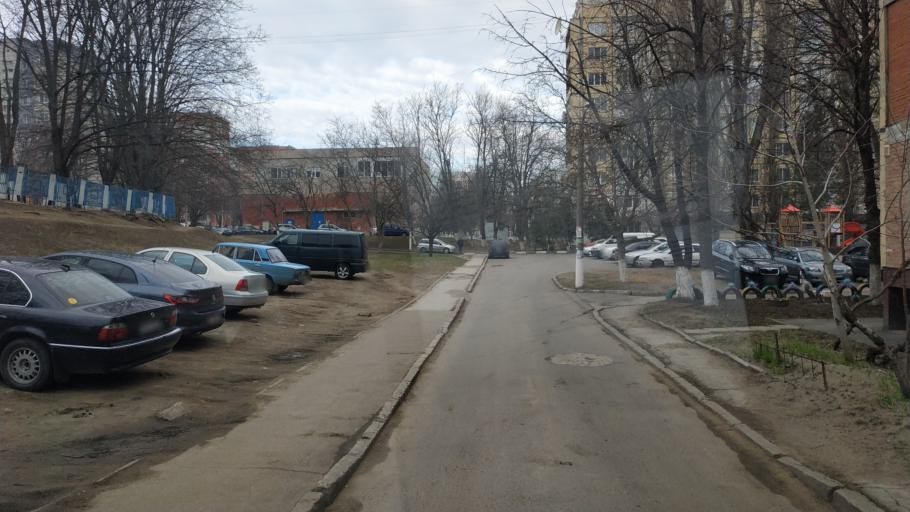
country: MD
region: Chisinau
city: Vatra
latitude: 47.0377
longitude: 28.7764
